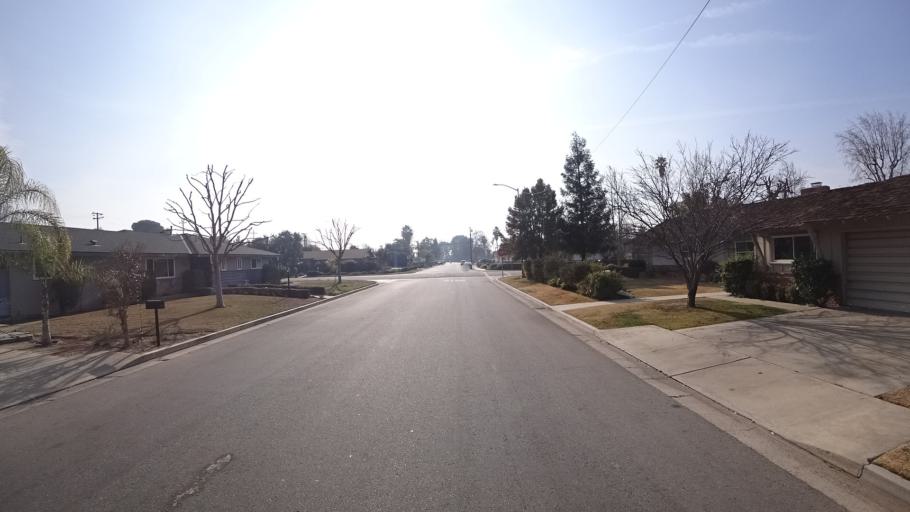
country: US
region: California
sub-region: Kern County
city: Bakersfield
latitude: 35.3632
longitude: -119.0469
